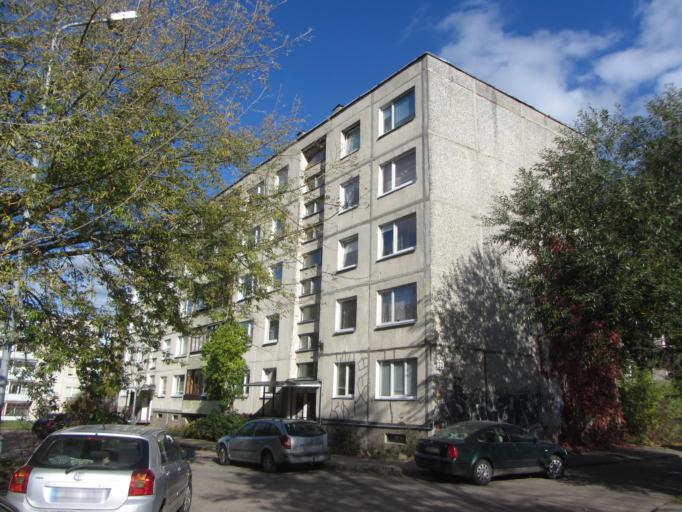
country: LT
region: Vilnius County
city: Lazdynai
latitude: 54.6732
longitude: 25.2054
